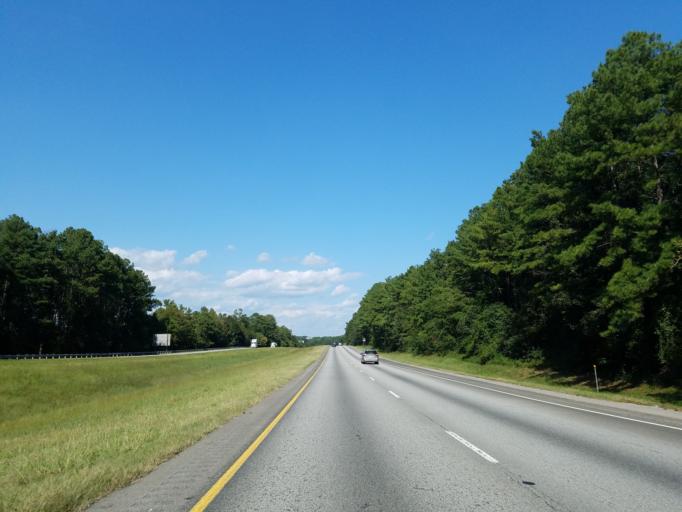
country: US
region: Georgia
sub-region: Franklin County
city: Carnesville
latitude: 34.3558
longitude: -83.3015
